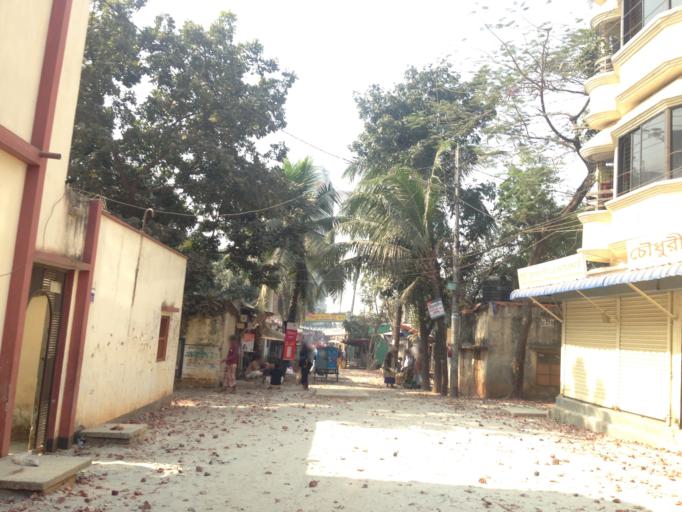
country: BD
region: Dhaka
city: Azimpur
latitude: 23.8047
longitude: 90.3456
